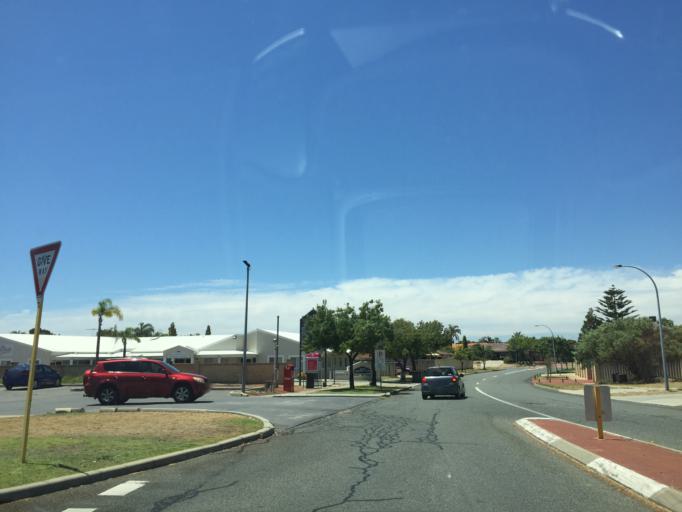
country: AU
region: Western Australia
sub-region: Melville
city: Winthrop
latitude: -32.0636
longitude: 115.8360
